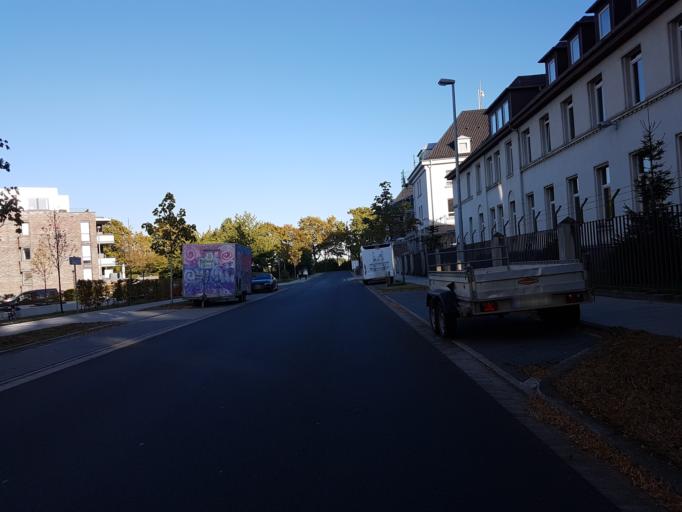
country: DE
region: Lower Saxony
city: Hannover
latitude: 52.4037
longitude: 9.7454
